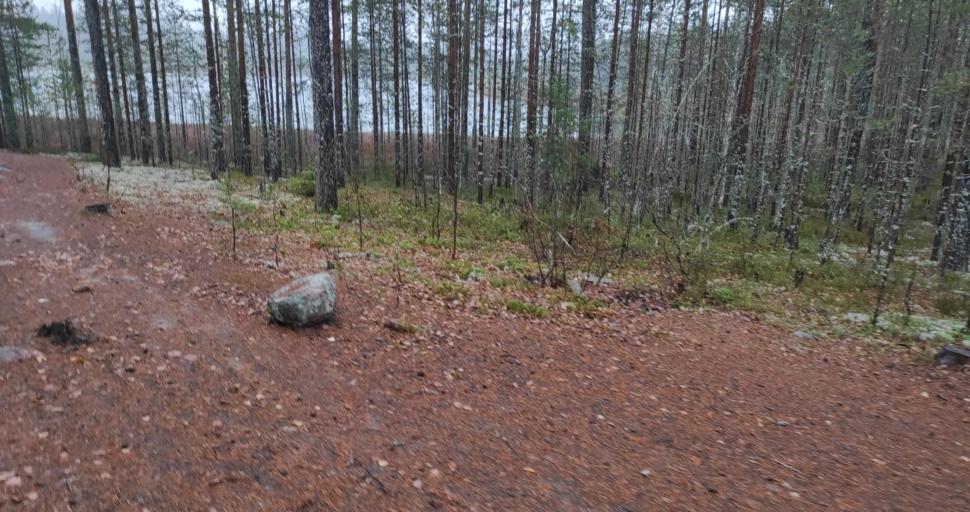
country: RU
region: Republic of Karelia
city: Salmi
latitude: 61.6251
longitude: 31.7652
